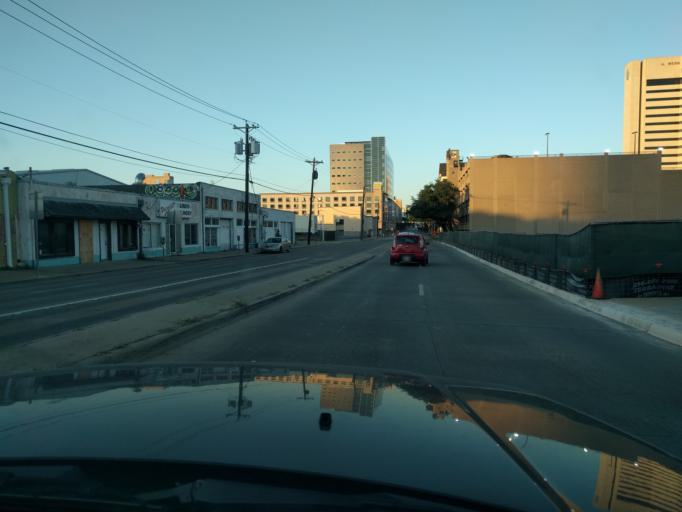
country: US
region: Texas
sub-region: Dallas County
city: Dallas
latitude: 32.7881
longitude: -96.7837
